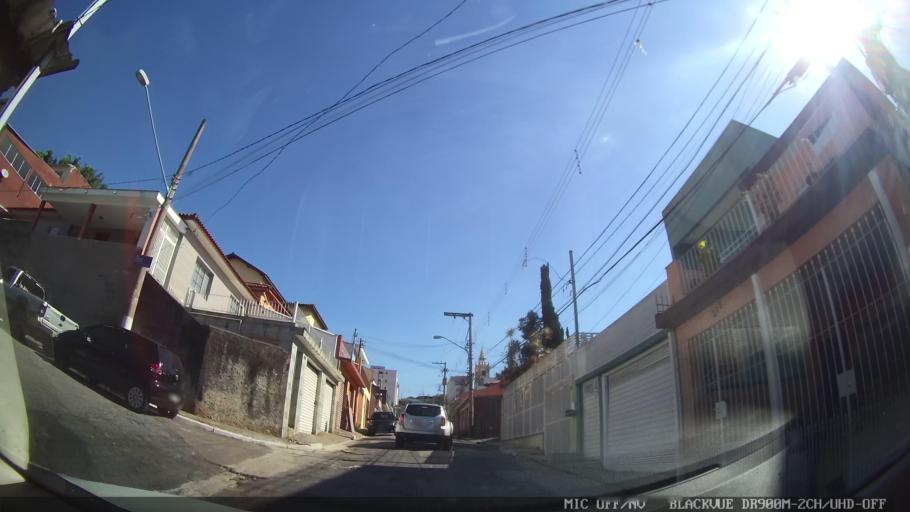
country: BR
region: Sao Paulo
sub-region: Sao Paulo
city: Sao Paulo
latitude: -23.4923
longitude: -46.6458
